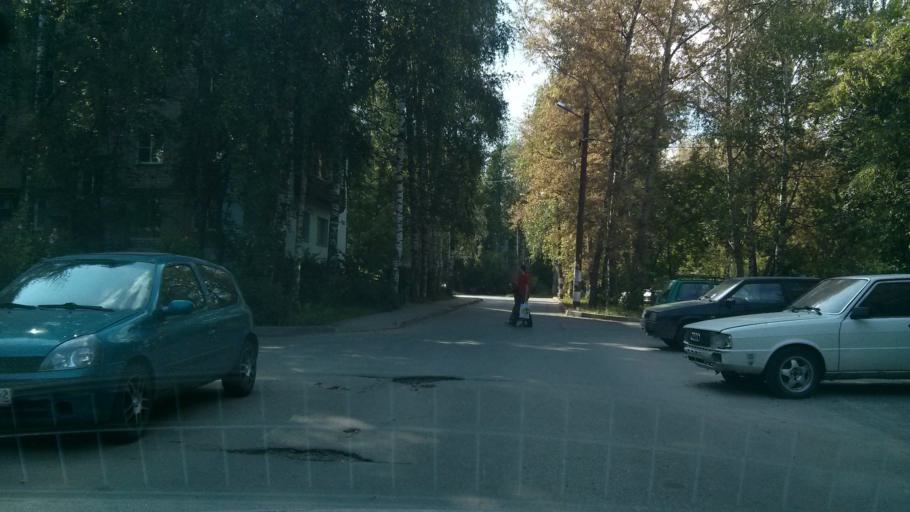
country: RU
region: Nizjnij Novgorod
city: Nizhniy Novgorod
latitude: 56.2933
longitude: 44.0457
